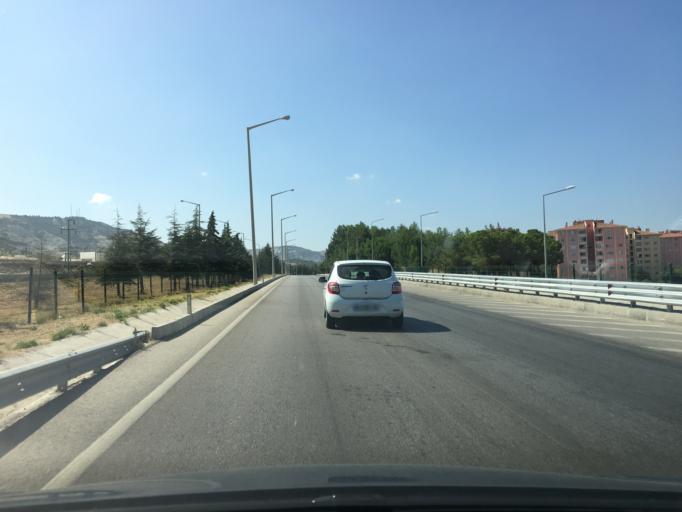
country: TR
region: Burdur
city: Burdur
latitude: 37.7374
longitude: 30.3113
